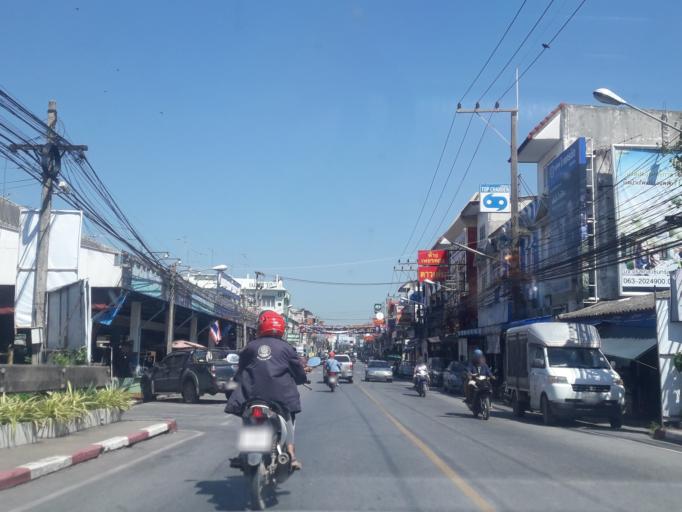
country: TH
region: Sara Buri
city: Nong Khae
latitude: 14.3407
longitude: 100.8669
